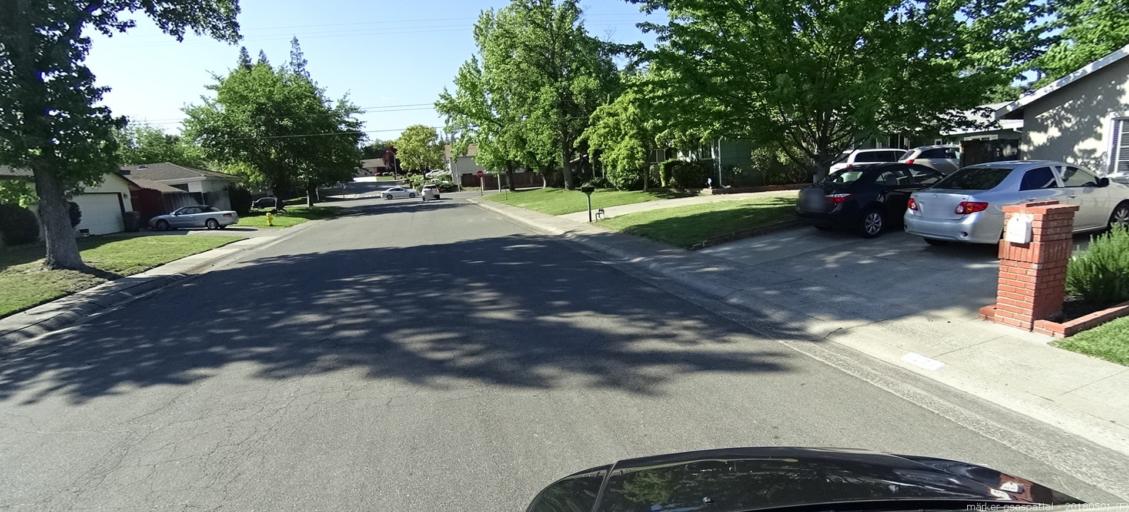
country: US
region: California
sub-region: Sacramento County
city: Foothill Farms
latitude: 38.6426
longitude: -121.3605
